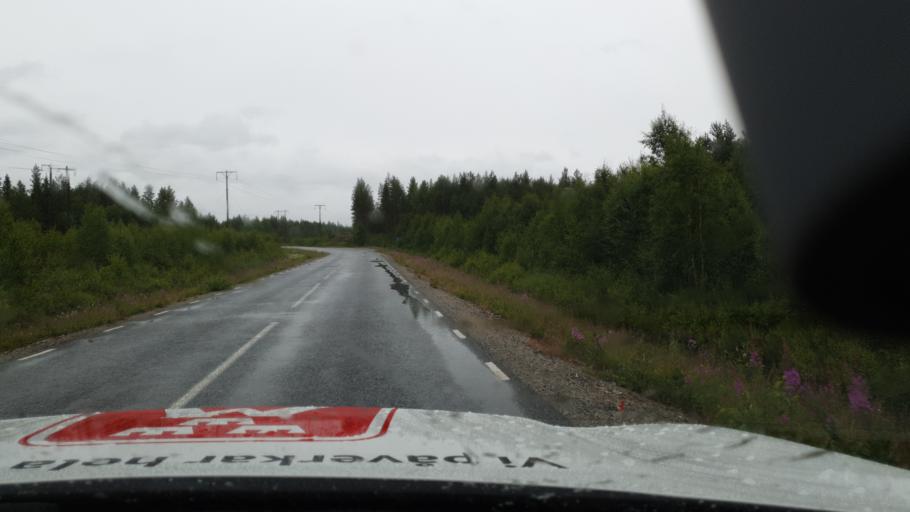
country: SE
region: Vaesterbotten
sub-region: Vindelns Kommun
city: Vindeln
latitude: 64.4240
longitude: 19.6999
